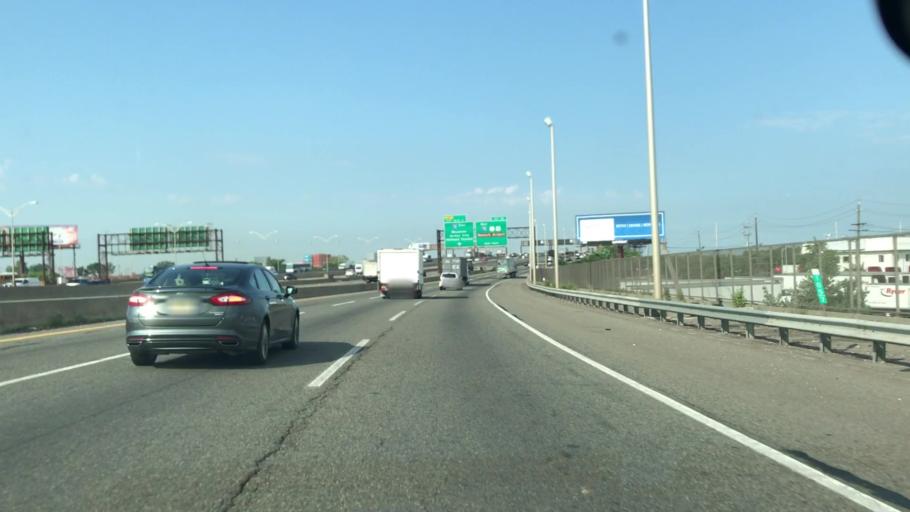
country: US
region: New Jersey
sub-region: Hudson County
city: Harrison
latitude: 40.7149
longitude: -74.1393
